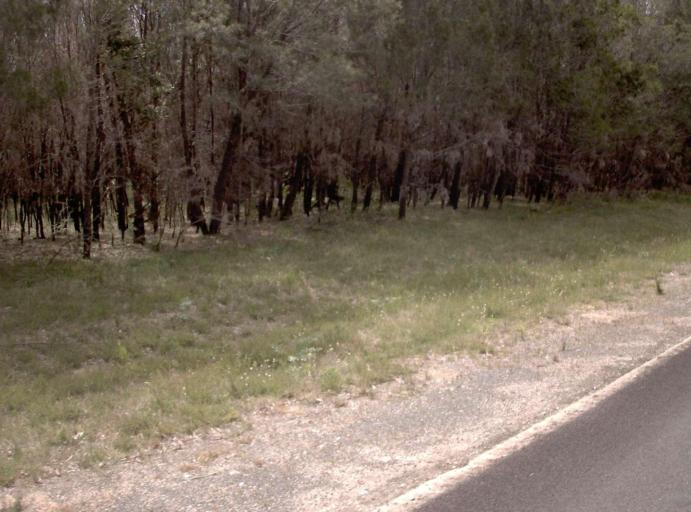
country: AU
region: New South Wales
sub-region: Bega Valley
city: Eden
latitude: -37.5194
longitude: 149.4967
